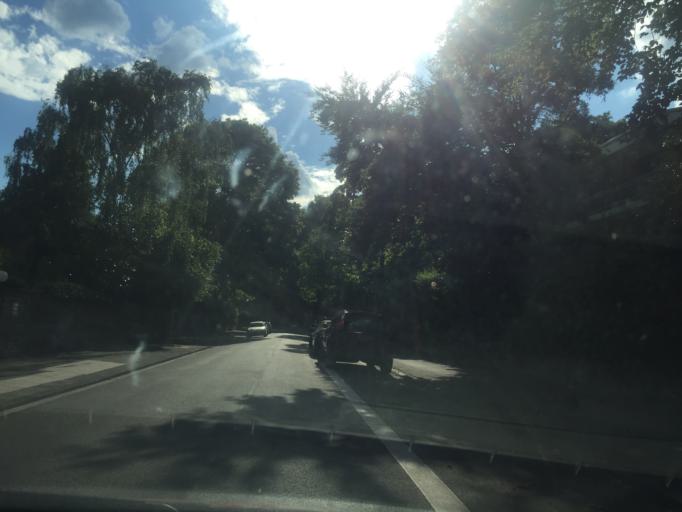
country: DE
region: North Rhine-Westphalia
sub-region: Regierungsbezirk Koln
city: Bayenthal
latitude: 50.9026
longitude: 6.9697
